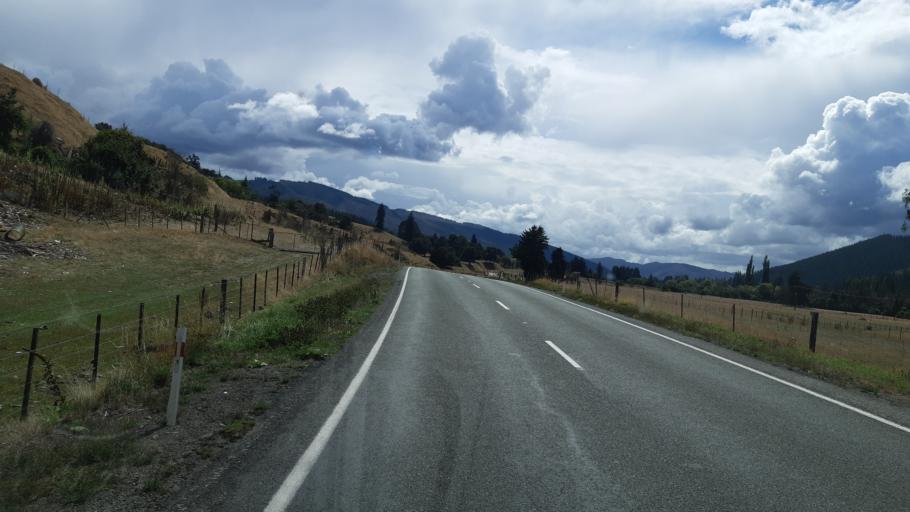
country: NZ
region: Tasman
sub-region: Tasman District
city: Wakefield
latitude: -41.4876
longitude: 172.7986
